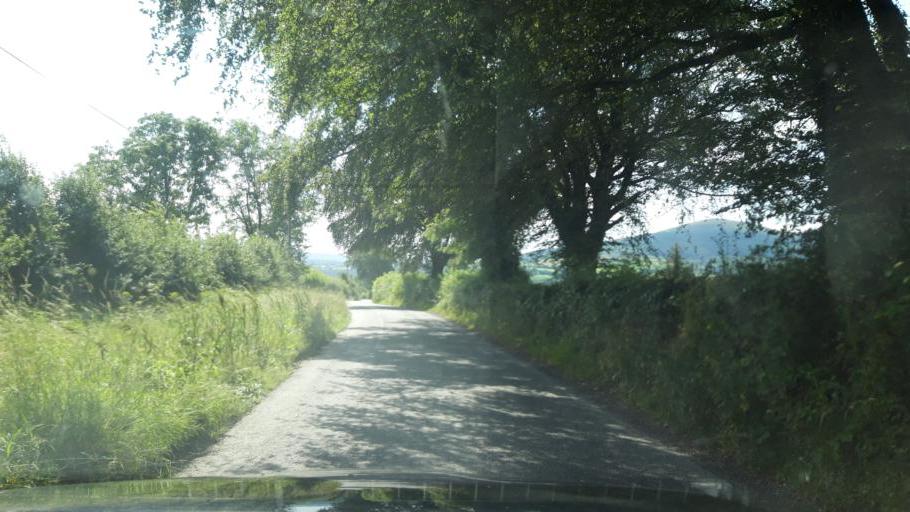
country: IE
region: Leinster
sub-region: Kilkenny
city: Graiguenamanagh
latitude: 52.5587
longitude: -6.9822
